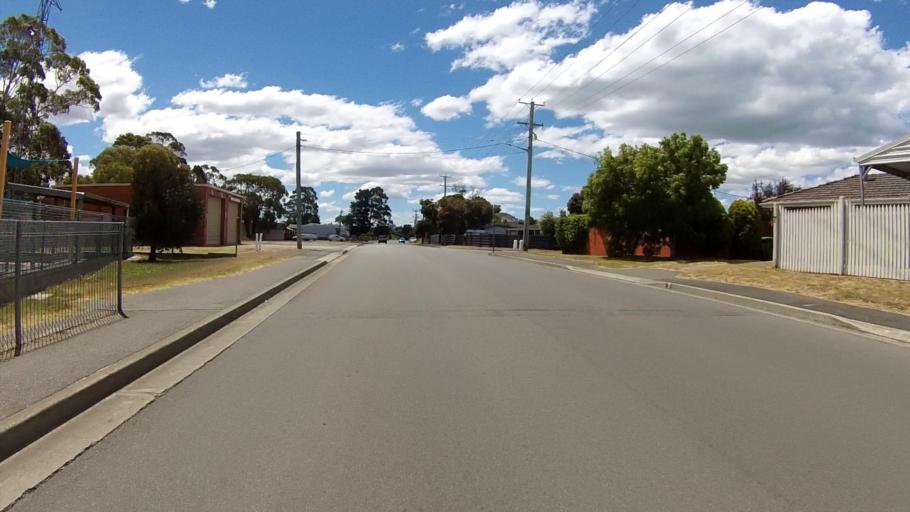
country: AU
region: Tasmania
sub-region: Clarence
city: Lauderdale
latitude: -42.9099
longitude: 147.4924
